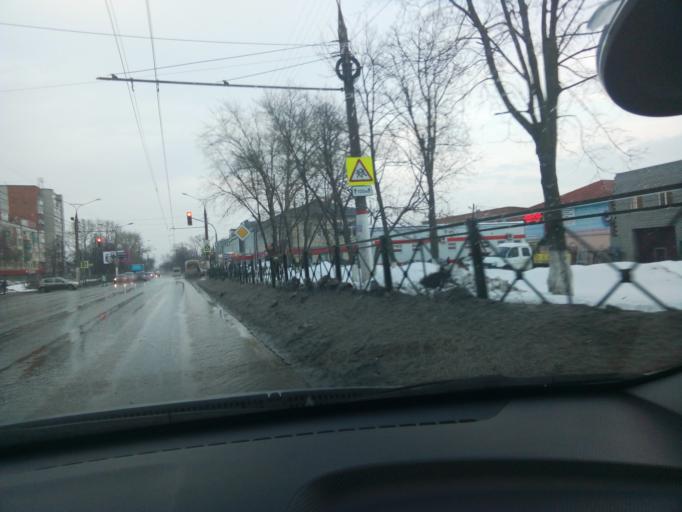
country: RU
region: Chuvashia
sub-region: Cheboksarskiy Rayon
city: Cheboksary
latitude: 56.1244
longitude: 47.2055
